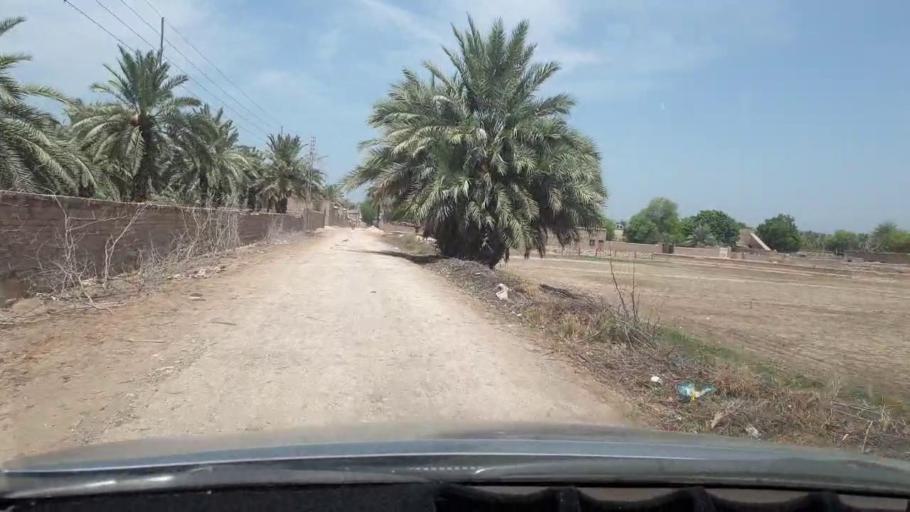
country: PK
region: Sindh
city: Khairpur
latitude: 27.4748
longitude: 68.7650
